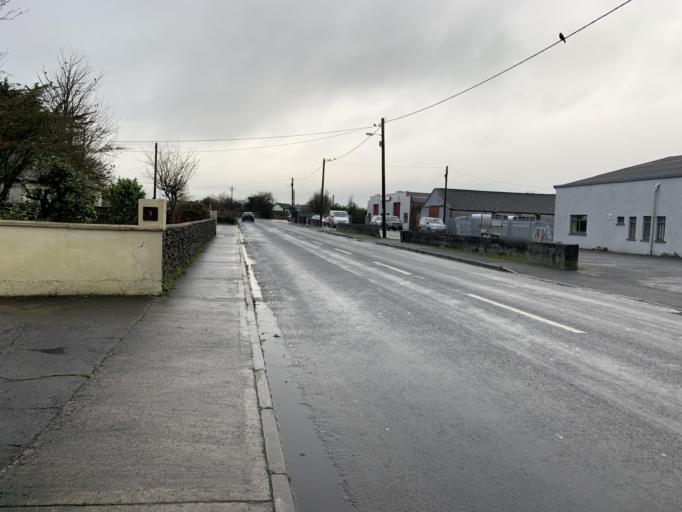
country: IE
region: Connaught
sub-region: County Galway
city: Tuam
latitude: 53.5131
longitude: -8.8614
